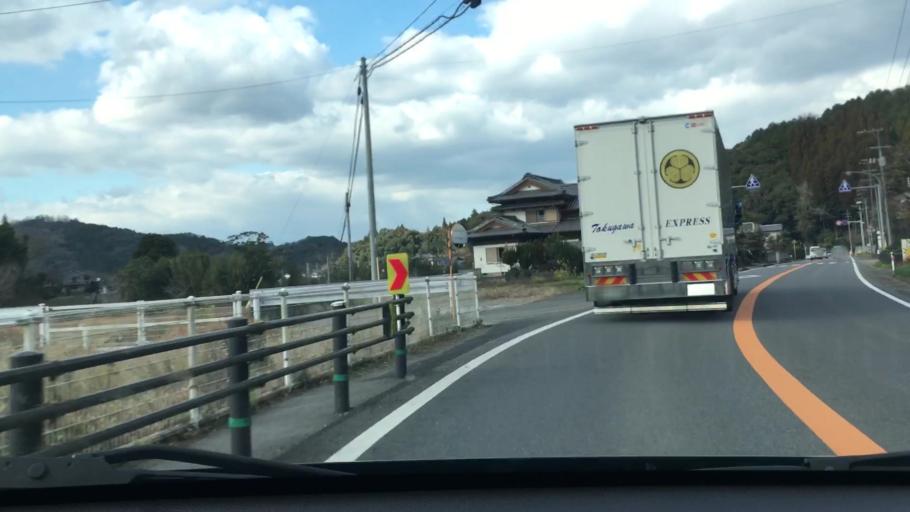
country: JP
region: Oita
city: Usuki
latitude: 33.0073
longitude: 131.7084
